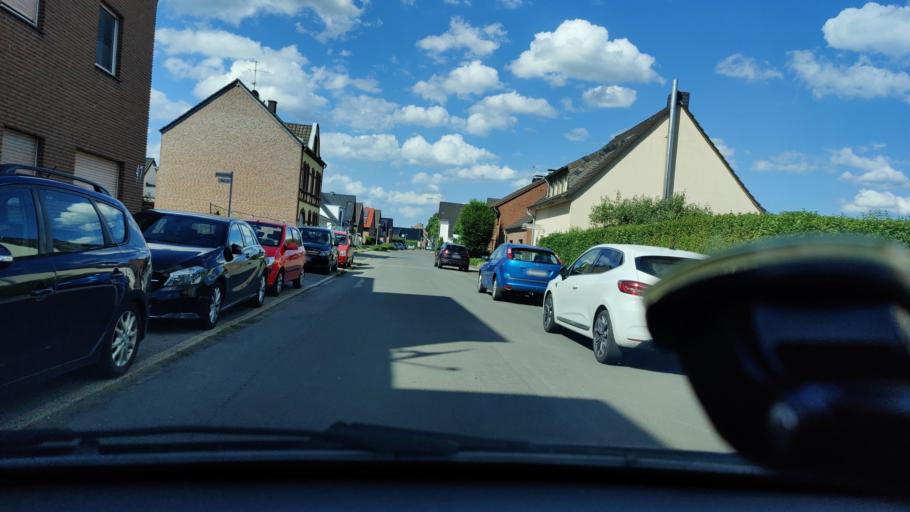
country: DE
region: North Rhine-Westphalia
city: Rheinberg
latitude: 51.5675
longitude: 6.5834
